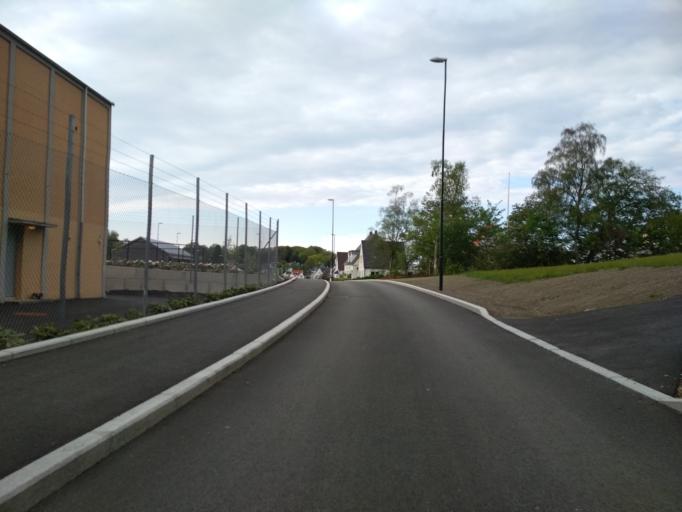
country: NO
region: Rogaland
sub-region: Stavanger
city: Stavanger
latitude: 58.9581
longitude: 5.7239
